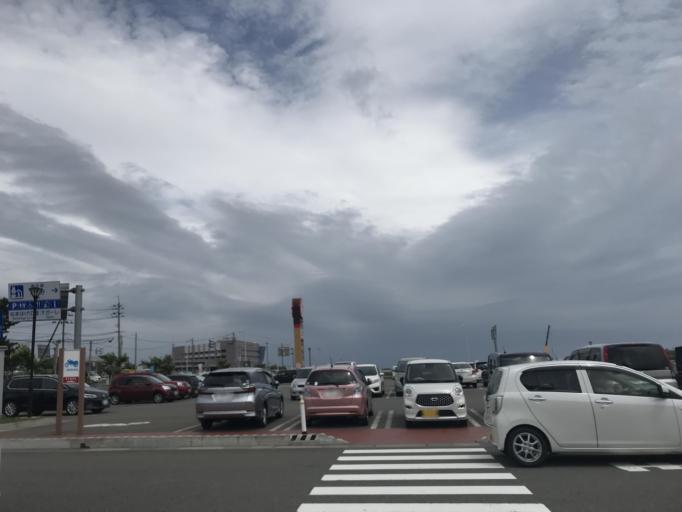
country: JP
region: Akita
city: Tenno
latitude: 39.8822
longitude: 139.8481
